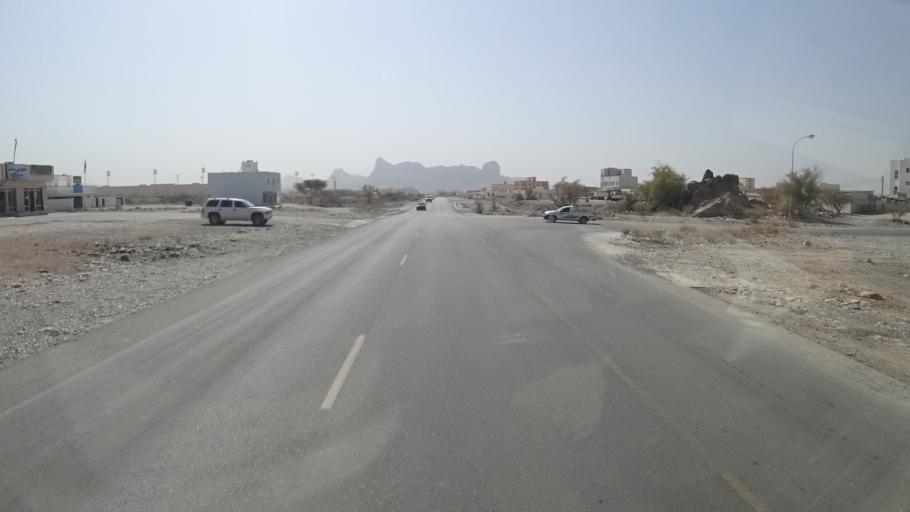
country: OM
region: Muhafazat ad Dakhiliyah
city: Bahla'
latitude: 23.1183
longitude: 57.2625
